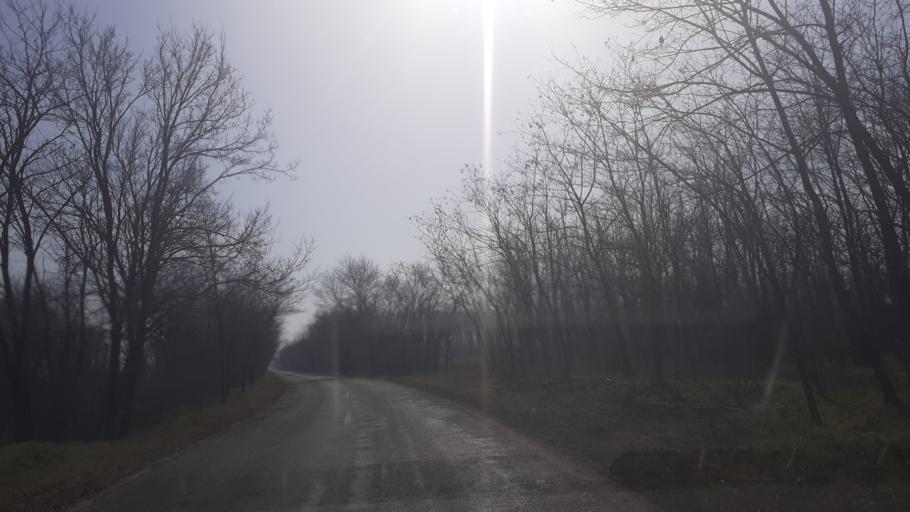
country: HU
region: Pest
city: Orkeny
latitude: 47.0946
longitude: 19.3608
